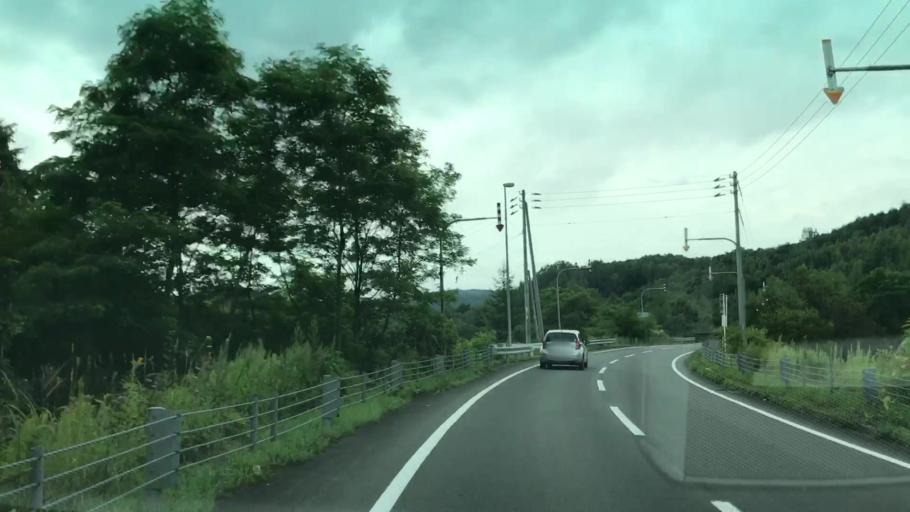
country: JP
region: Hokkaido
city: Yoichi
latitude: 43.1492
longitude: 140.8222
